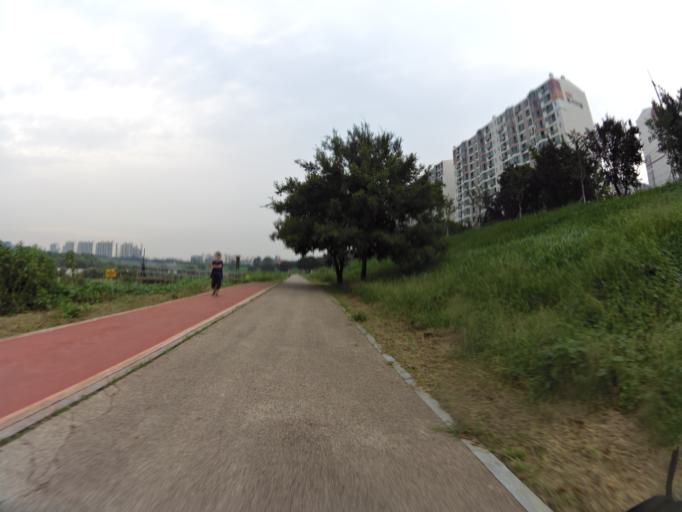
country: KR
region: Gyeongsangbuk-do
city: Gyeongsan-si
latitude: 35.8720
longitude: 128.6791
